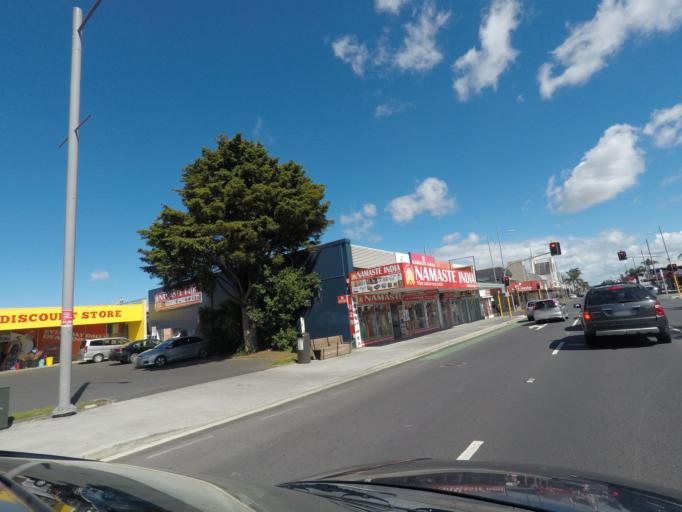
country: NZ
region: Auckland
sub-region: Auckland
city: Wiri
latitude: -36.9713
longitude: 174.8622
